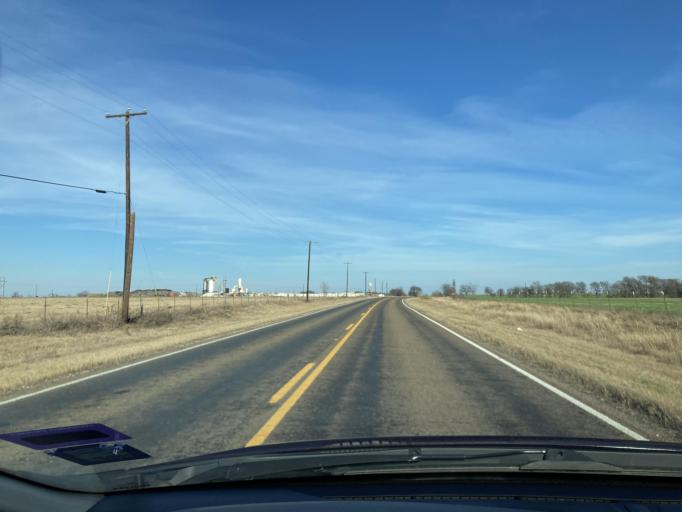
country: US
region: Texas
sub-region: Navarro County
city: Corsicana
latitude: 32.0231
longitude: -96.4172
